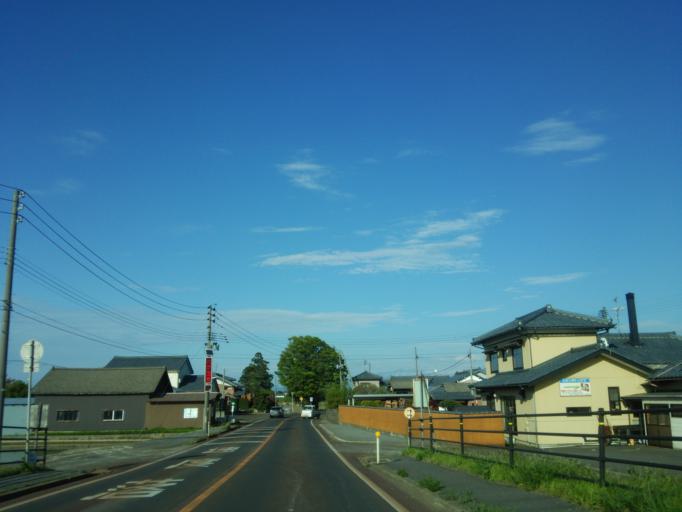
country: JP
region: Niigata
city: Niitsu-honcho
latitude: 37.8132
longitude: 139.1619
